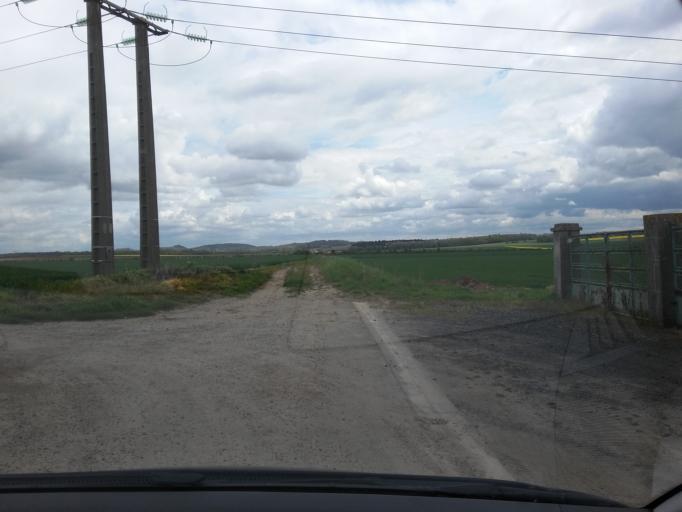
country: FR
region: Picardie
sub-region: Departement de l'Oise
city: Grandfresnoy
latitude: 49.3652
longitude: 2.6633
